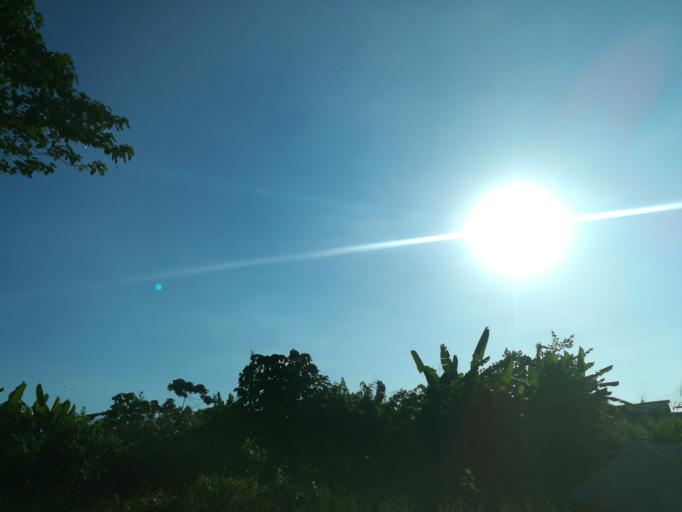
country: NG
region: Lagos
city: Ikorodu
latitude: 6.5676
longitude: 3.5340
